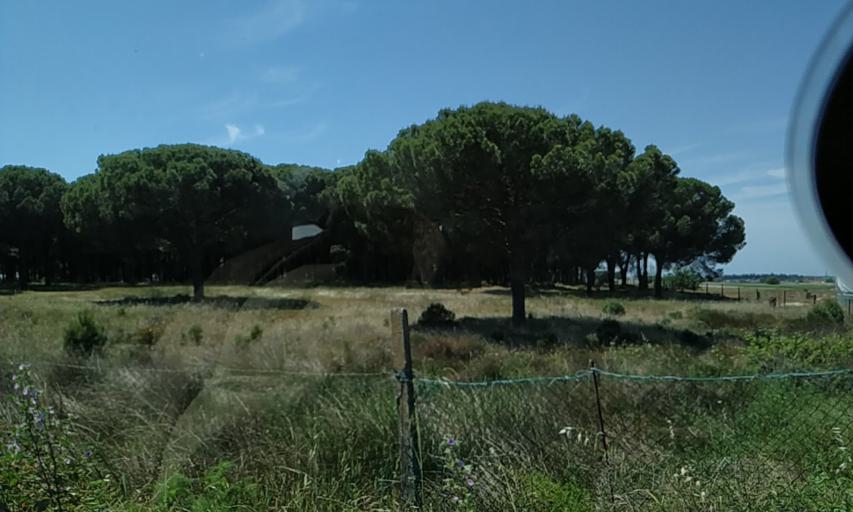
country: PT
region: Santarem
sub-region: Benavente
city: Poceirao
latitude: 38.6906
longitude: -8.7302
